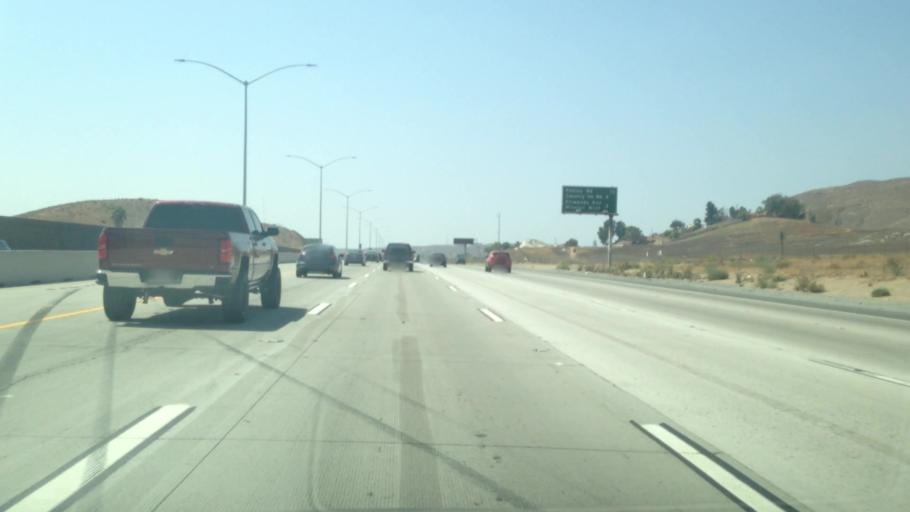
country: US
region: California
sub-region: Riverside County
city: Glen Avon
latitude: 34.0173
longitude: -117.4702
